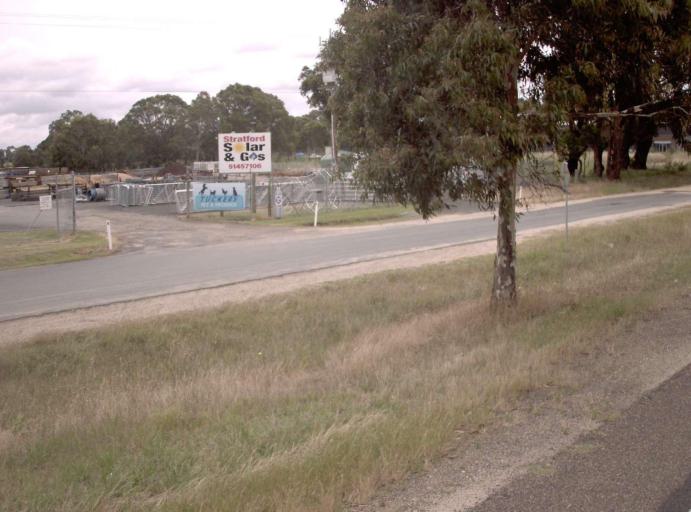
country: AU
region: Victoria
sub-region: Wellington
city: Sale
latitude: -37.9620
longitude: 147.0903
